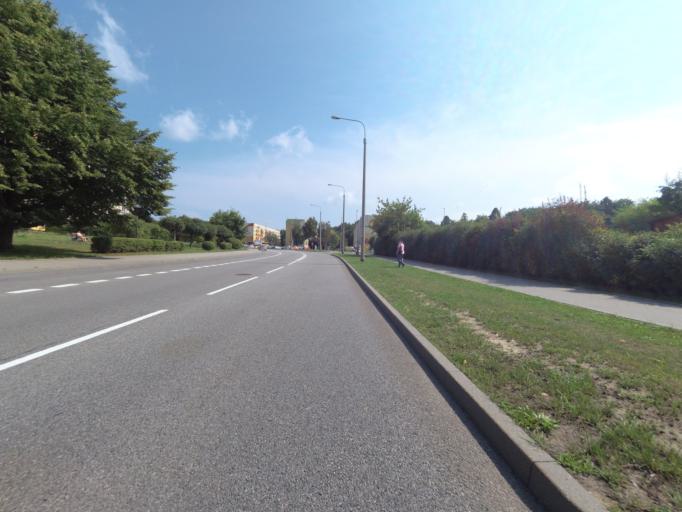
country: PL
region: Pomeranian Voivodeship
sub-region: Gdynia
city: Wielki Kack
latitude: 54.4926
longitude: 18.5083
